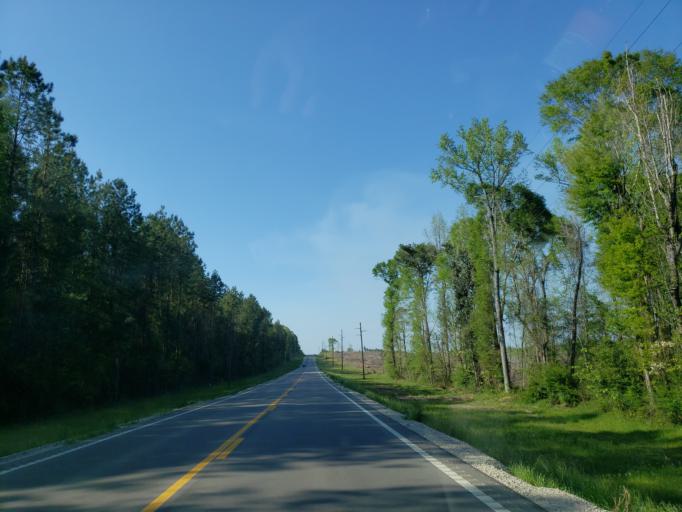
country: US
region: Mississippi
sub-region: Perry County
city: Richton
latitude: 31.2885
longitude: -88.9235
